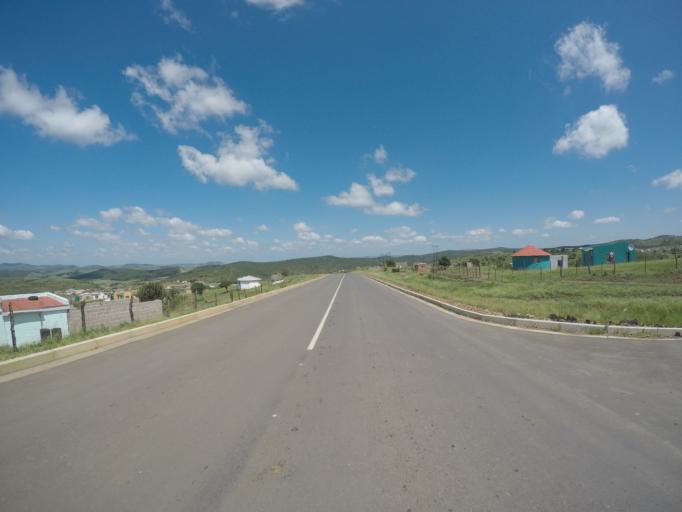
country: ZA
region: KwaZulu-Natal
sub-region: uThungulu District Municipality
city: Empangeni
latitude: -28.6081
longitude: 31.7466
